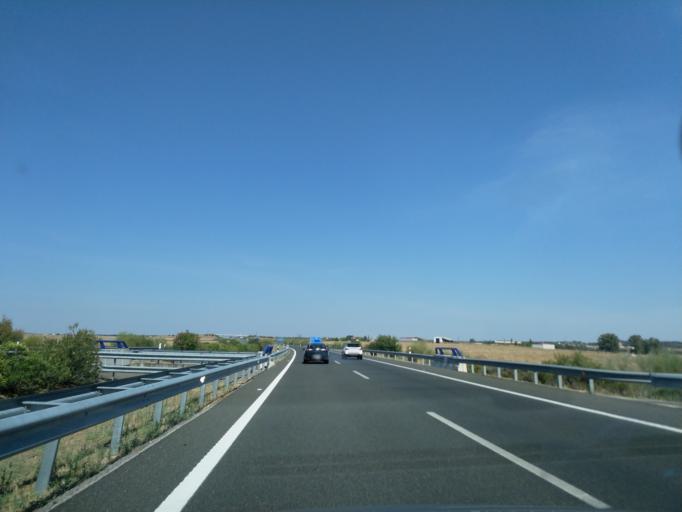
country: ES
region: Extremadura
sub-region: Provincia de Caceres
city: Aldea del Cano
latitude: 39.2749
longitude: -6.3231
